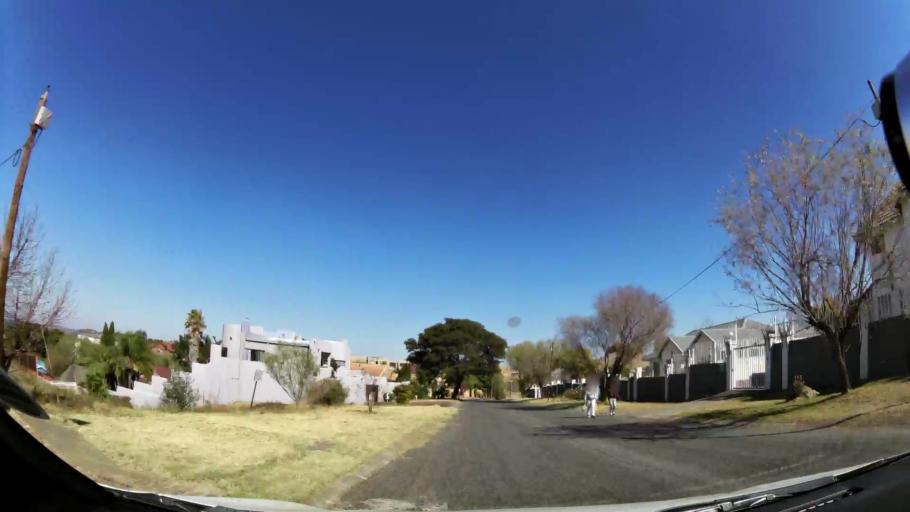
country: ZA
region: Gauteng
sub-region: City of Johannesburg Metropolitan Municipality
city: Johannesburg
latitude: -26.2620
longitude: 27.9979
